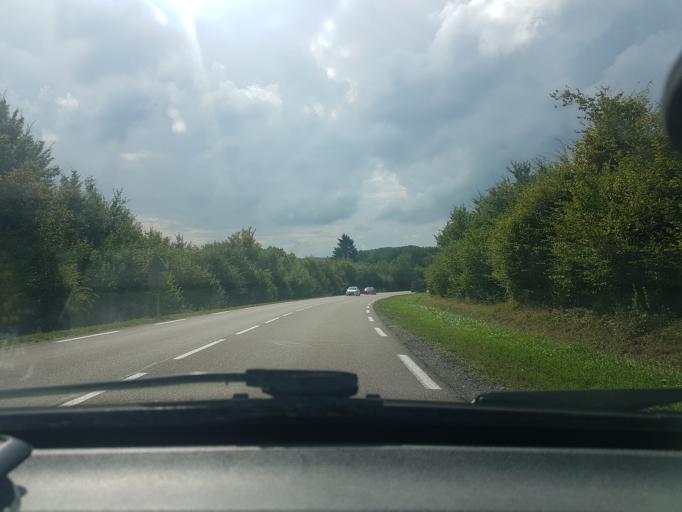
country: FR
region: Franche-Comte
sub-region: Departement de la Haute-Saone
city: Hericourt
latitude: 47.5942
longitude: 6.7185
